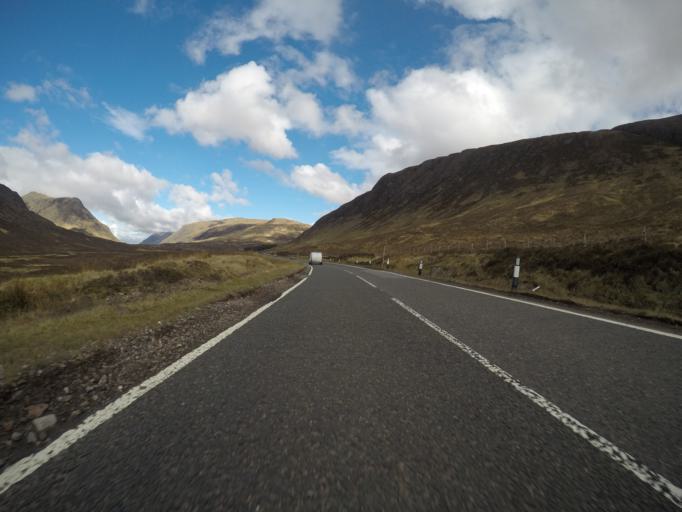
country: GB
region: Scotland
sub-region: Highland
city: Spean Bridge
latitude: 56.6577
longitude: -4.8792
